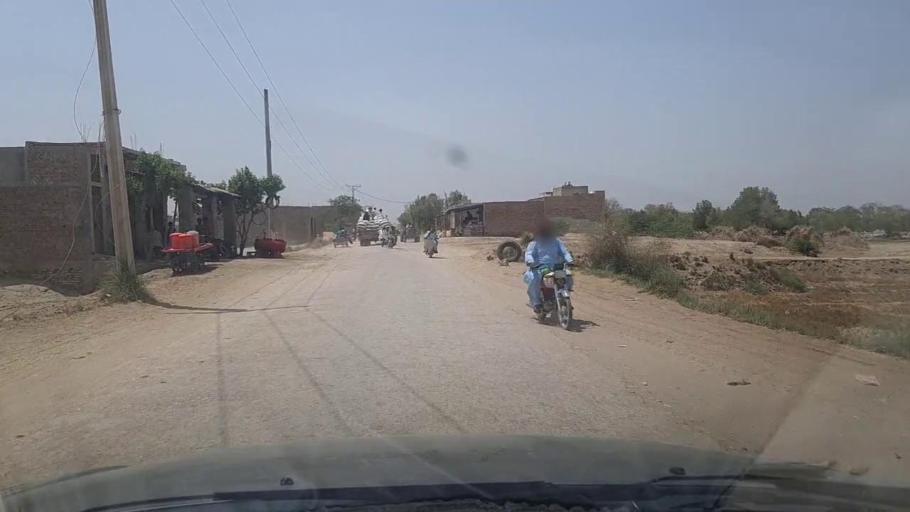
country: PK
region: Sindh
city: Bhiria
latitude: 26.8837
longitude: 68.2931
